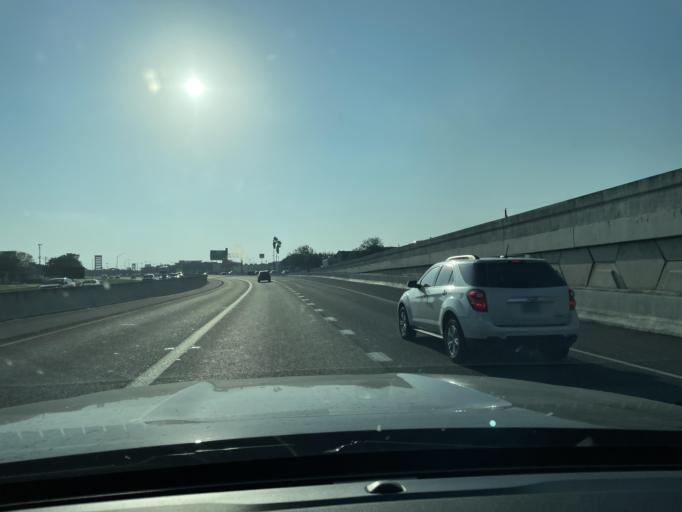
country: US
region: Texas
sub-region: Nueces County
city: Robstown
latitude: 27.8615
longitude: -97.6267
